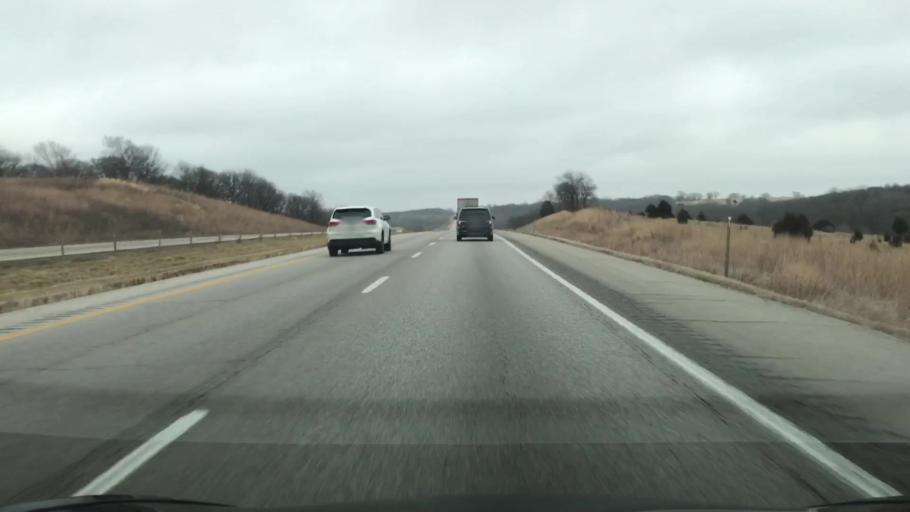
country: US
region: Iowa
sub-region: Madison County
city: Earlham
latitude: 41.5176
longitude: -94.1592
